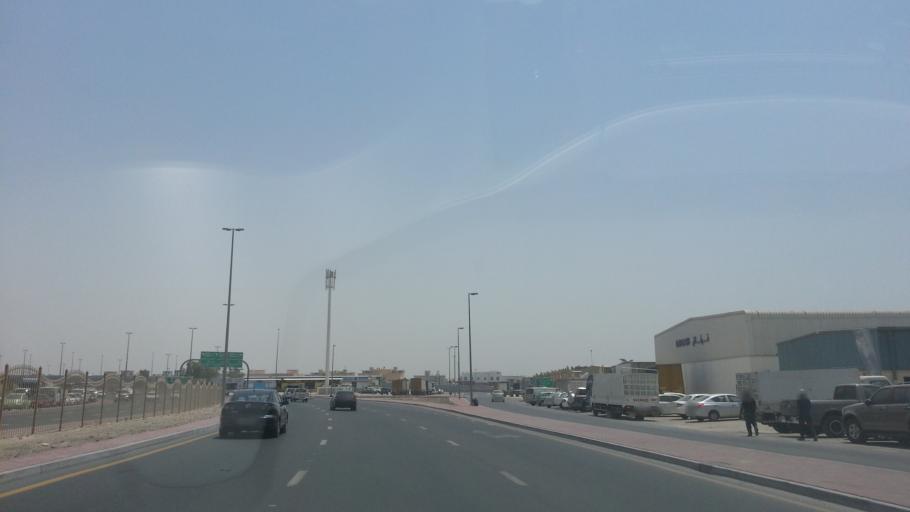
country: AE
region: Dubai
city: Dubai
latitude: 25.1150
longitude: 55.2206
